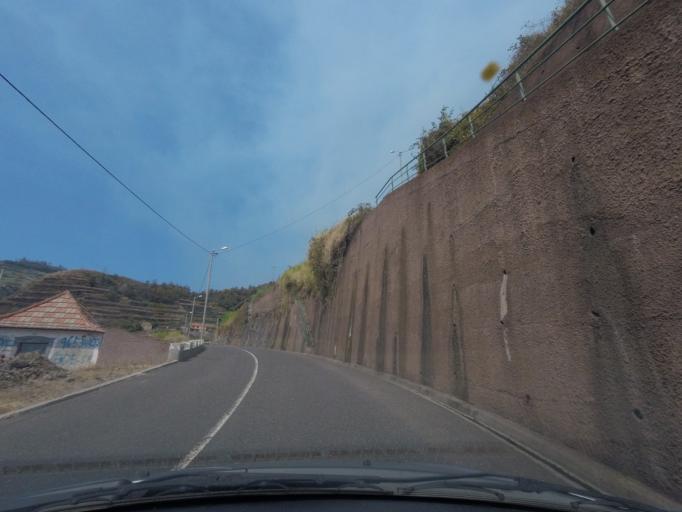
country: PT
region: Madeira
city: Ponta do Sol
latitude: 32.6866
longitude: -17.0698
